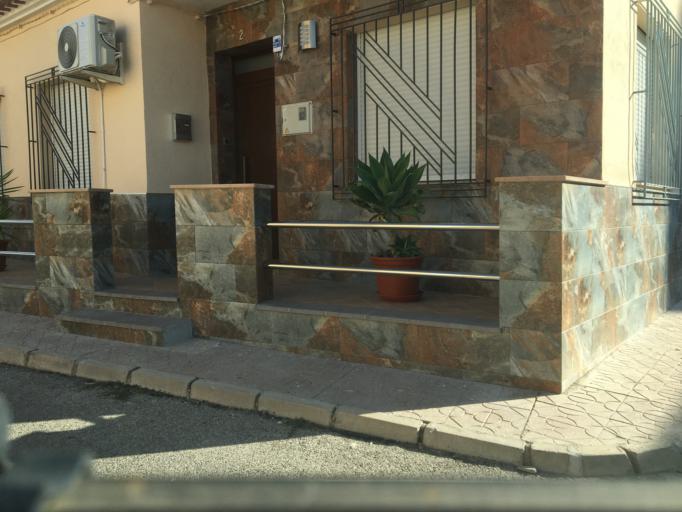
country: ES
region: Murcia
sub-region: Murcia
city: Puerto Lumbreras
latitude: 37.5577
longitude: -1.8121
